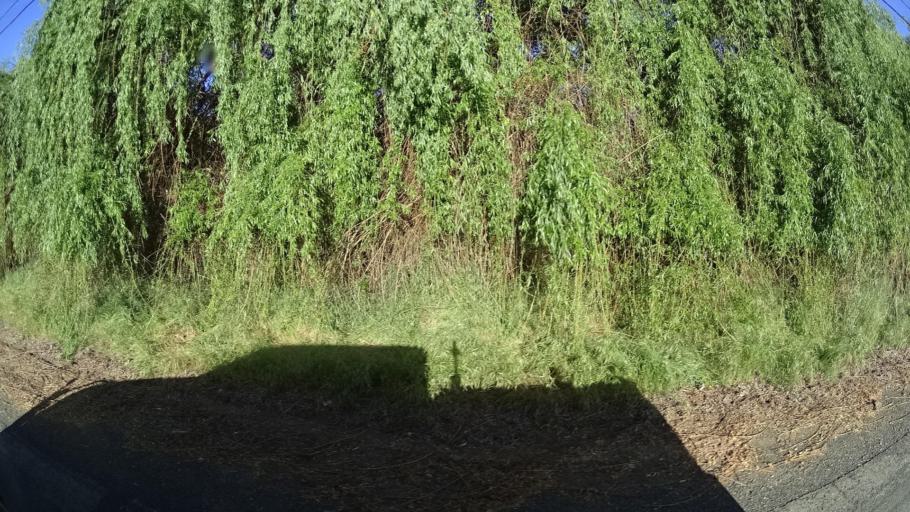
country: US
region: California
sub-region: Lake County
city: Lakeport
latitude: 39.0641
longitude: -122.9496
